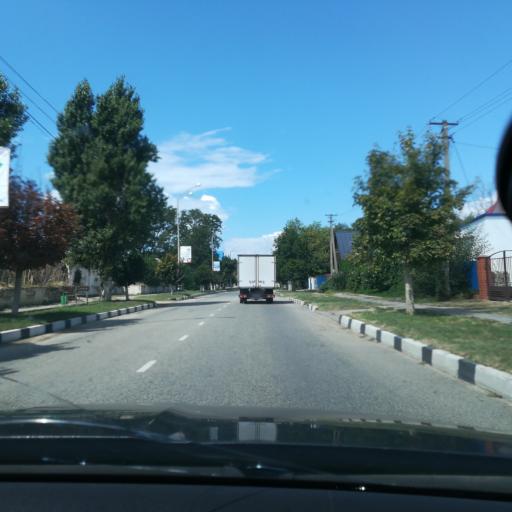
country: RU
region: Krasnodarskiy
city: Taman'
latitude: 45.2173
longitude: 36.7277
